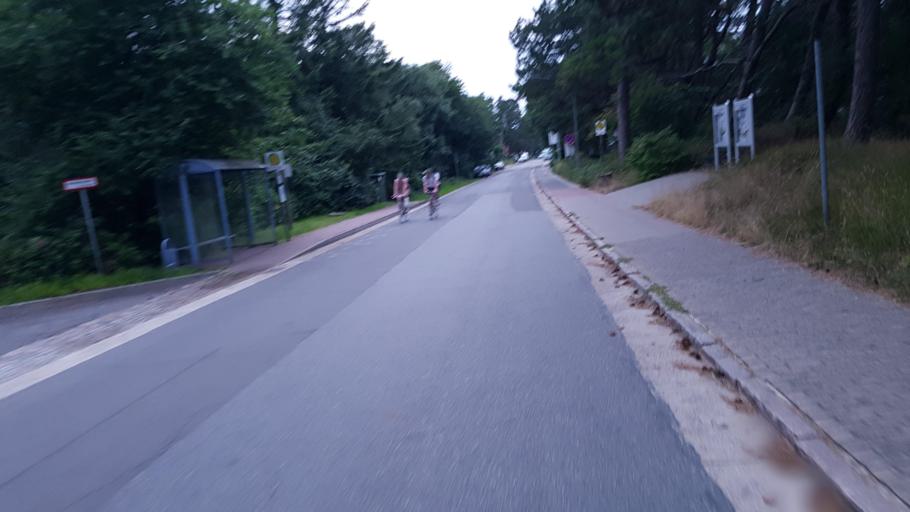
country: DE
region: Schleswig-Holstein
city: Sankt Peter-Ording
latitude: 54.3079
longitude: 8.6191
